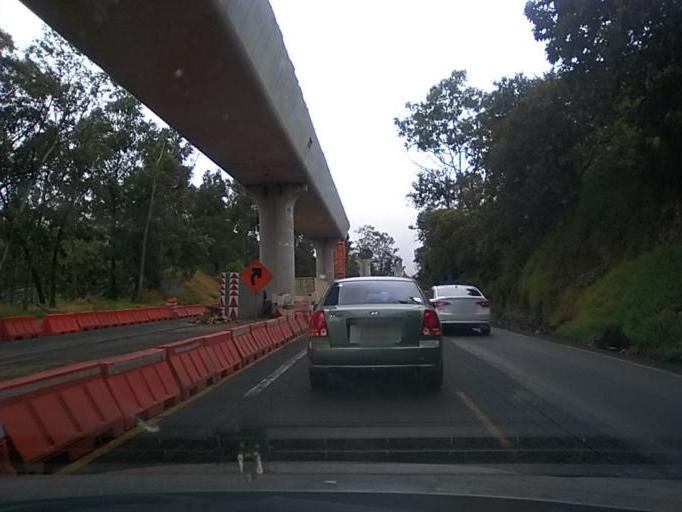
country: MX
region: Mexico City
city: Xochimilco
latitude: 19.2459
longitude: -99.1518
